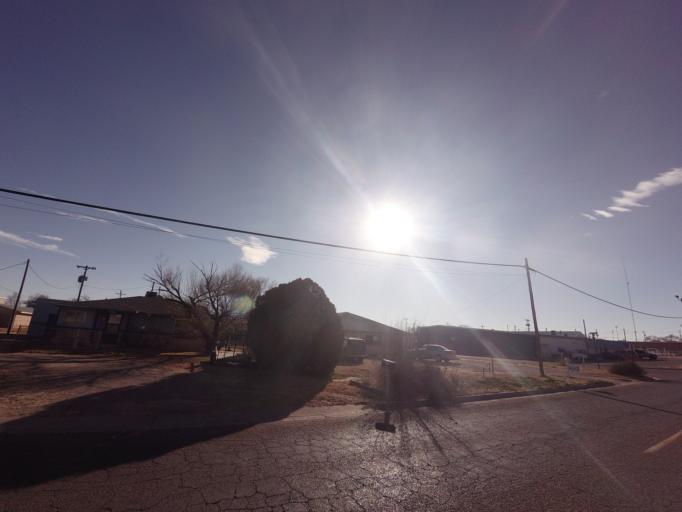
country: US
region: New Mexico
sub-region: Curry County
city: Clovis
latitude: 34.4048
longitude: -103.1848
